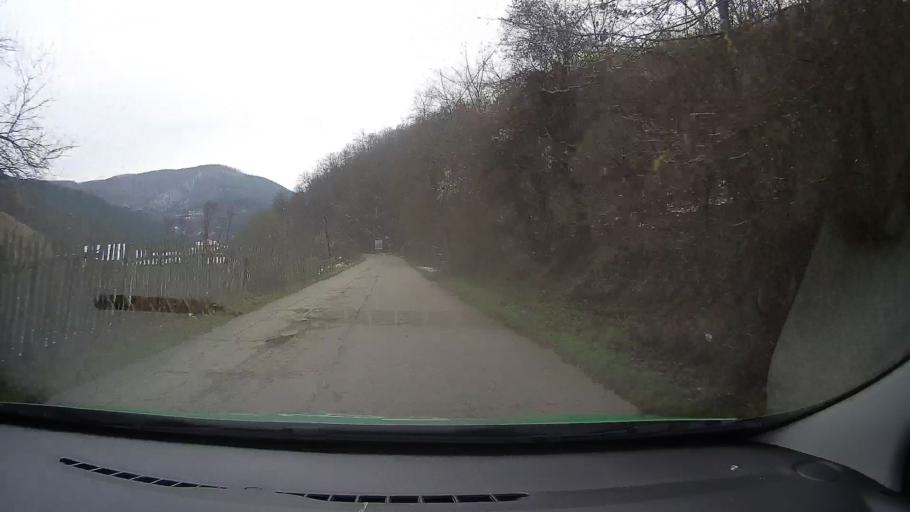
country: RO
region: Hunedoara
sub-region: Comuna Balsa
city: Balsa
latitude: 45.9808
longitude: 23.1645
